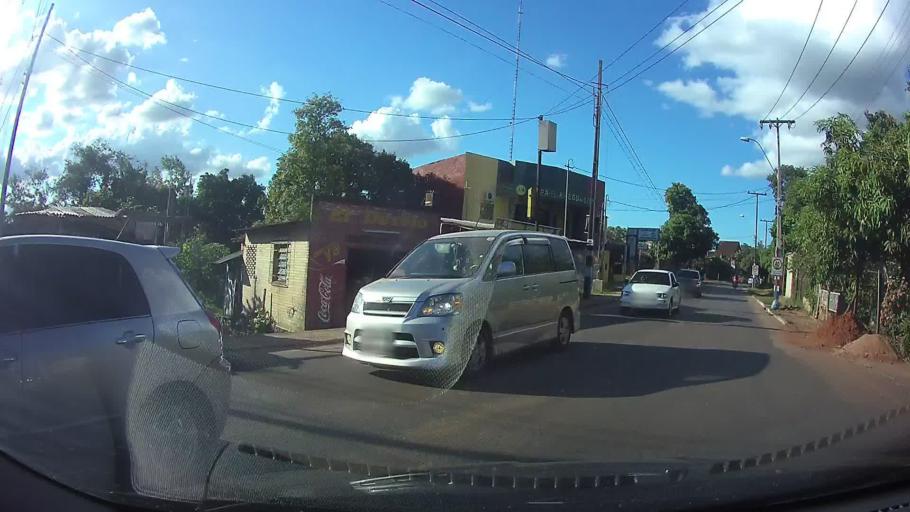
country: PY
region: Central
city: Aregua
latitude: -25.2928
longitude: -57.4414
